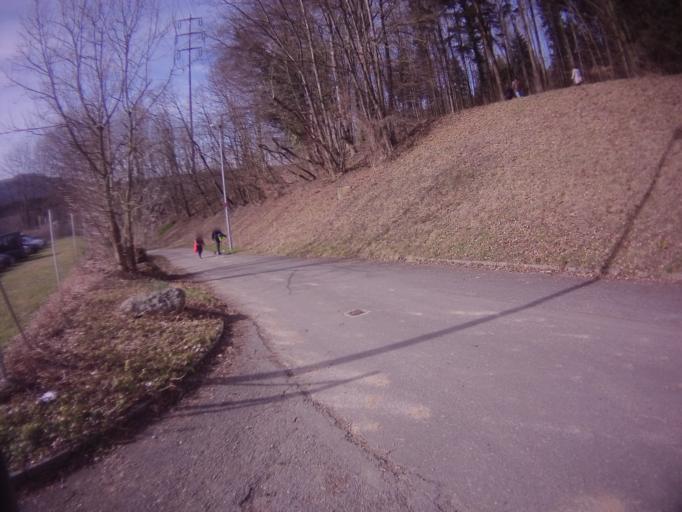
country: CH
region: Aargau
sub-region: Bezirk Baden
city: Killwangen
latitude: 47.4397
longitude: 8.3474
